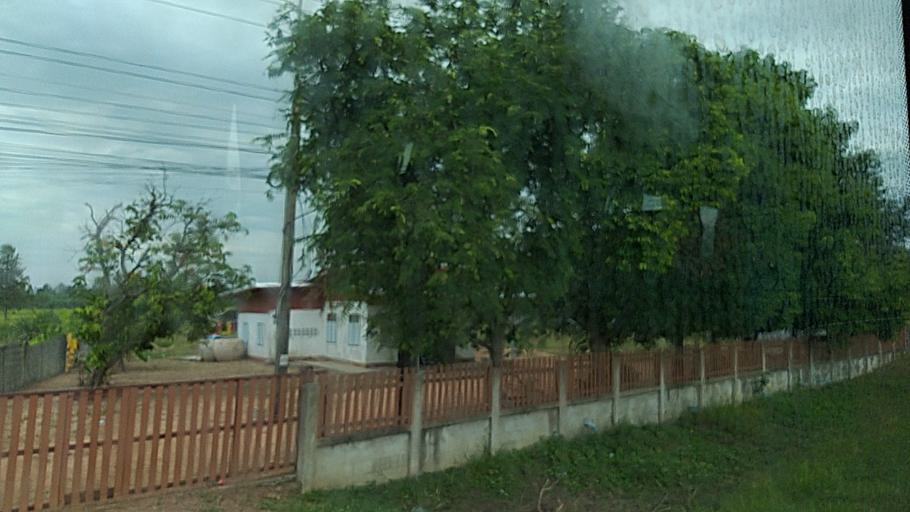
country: TH
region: Maha Sarakham
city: Kantharawichai
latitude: 16.3382
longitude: 103.1969
